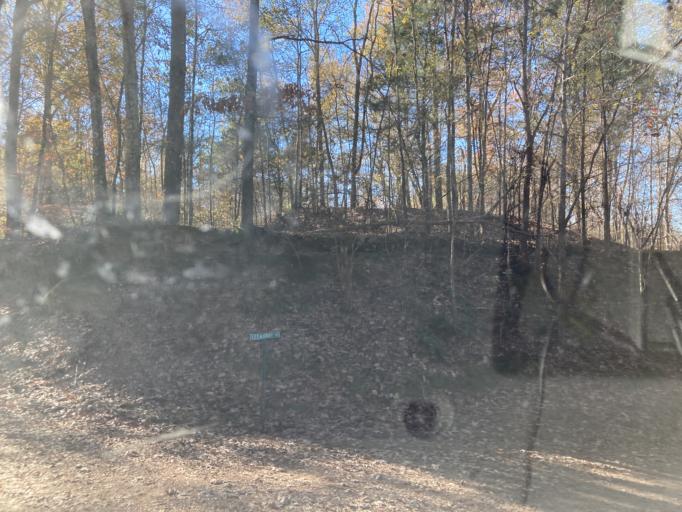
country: US
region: Mississippi
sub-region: Madison County
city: Kearney Park
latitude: 32.6187
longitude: -90.4567
